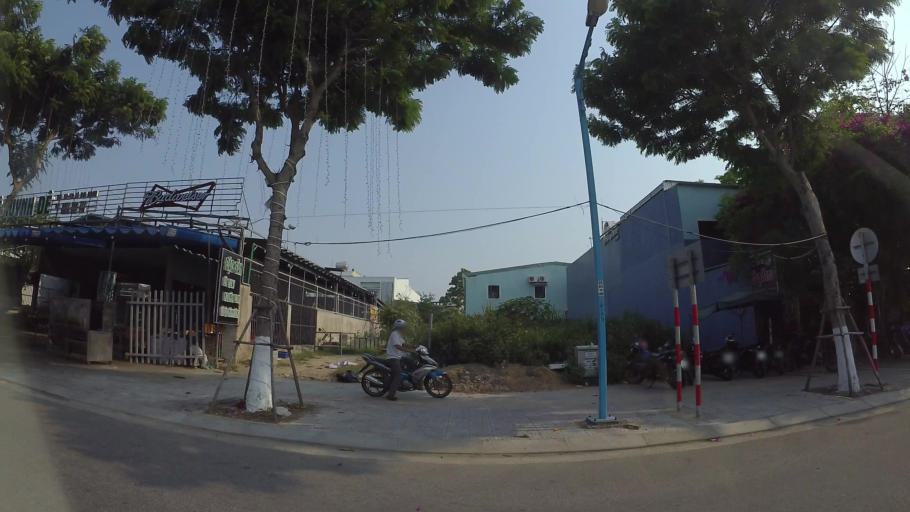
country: VN
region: Da Nang
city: Cam Le
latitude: 16.0234
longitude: 108.2048
